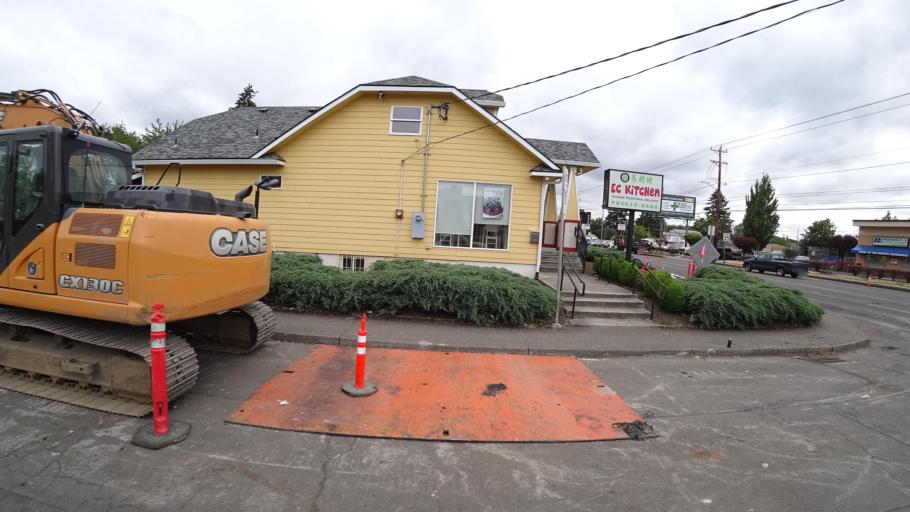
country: US
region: Oregon
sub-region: Multnomah County
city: Lents
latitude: 45.4768
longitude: -122.5794
